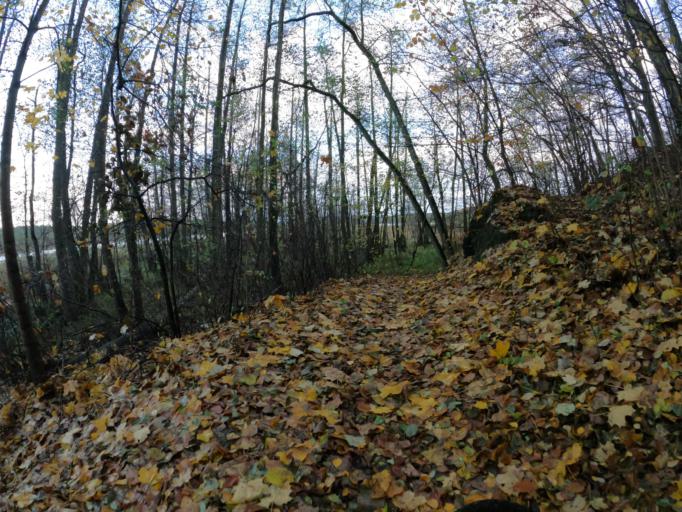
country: PL
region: West Pomeranian Voivodeship
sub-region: Powiat walecki
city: Tuczno
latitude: 53.1879
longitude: 16.1709
